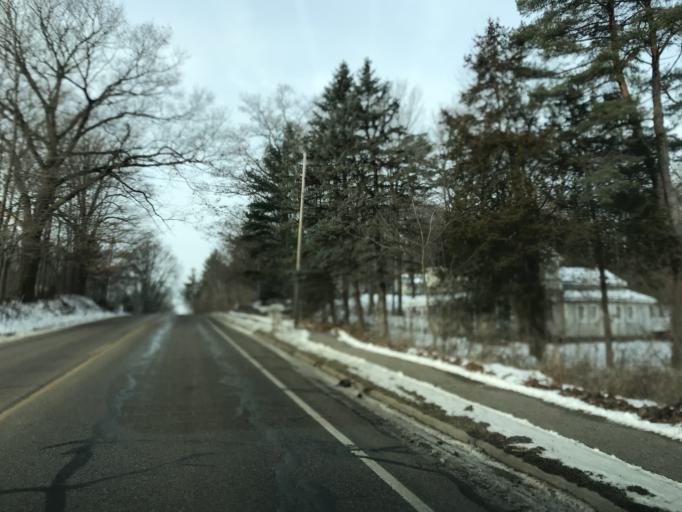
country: US
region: Michigan
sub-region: Kent County
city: Byron Center
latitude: 42.7252
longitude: -85.7360
